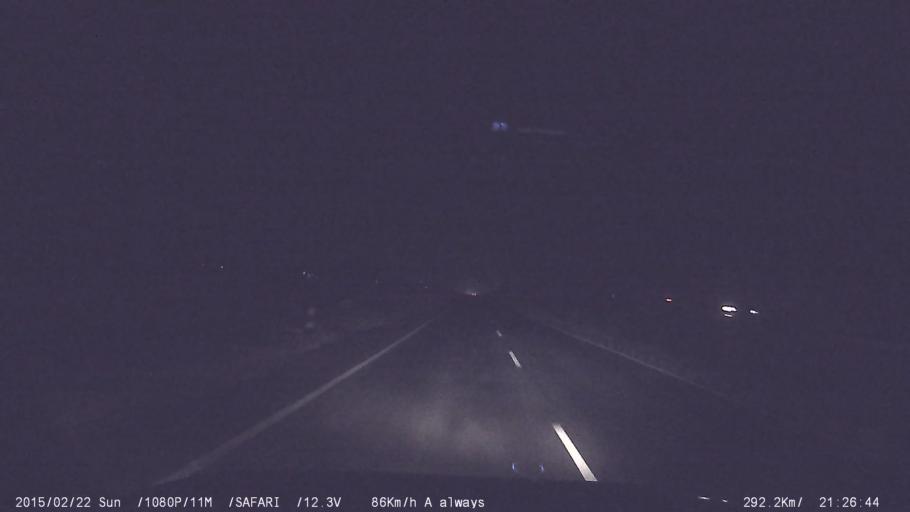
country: IN
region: Tamil Nadu
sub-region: Karur
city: Karur
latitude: 10.9085
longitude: 78.0382
